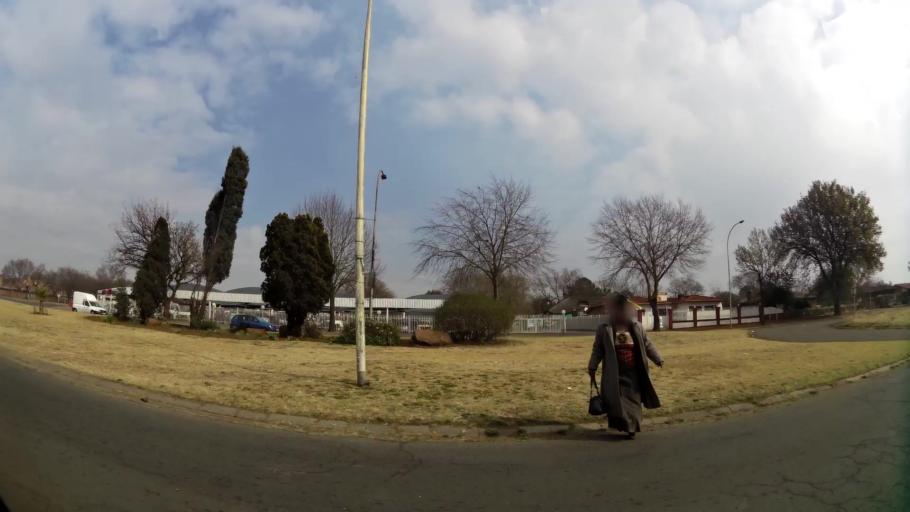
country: ZA
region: Gauteng
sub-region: Sedibeng District Municipality
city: Vanderbijlpark
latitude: -26.6829
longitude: 27.8348
